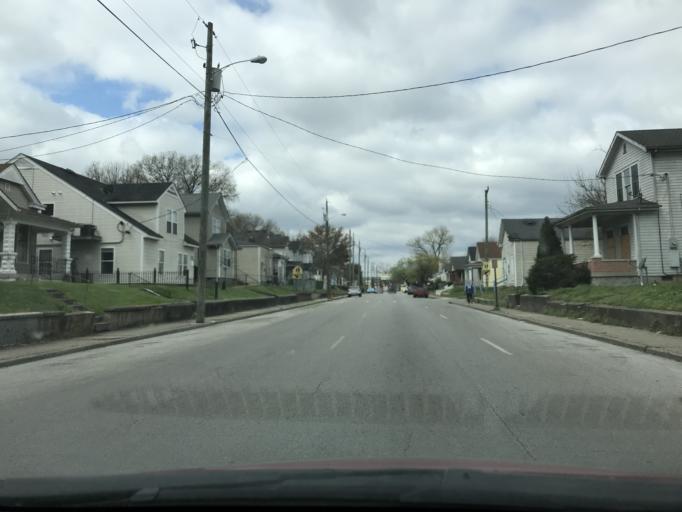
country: US
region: Kentucky
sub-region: Jefferson County
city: Louisville
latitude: 38.2371
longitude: -85.7832
